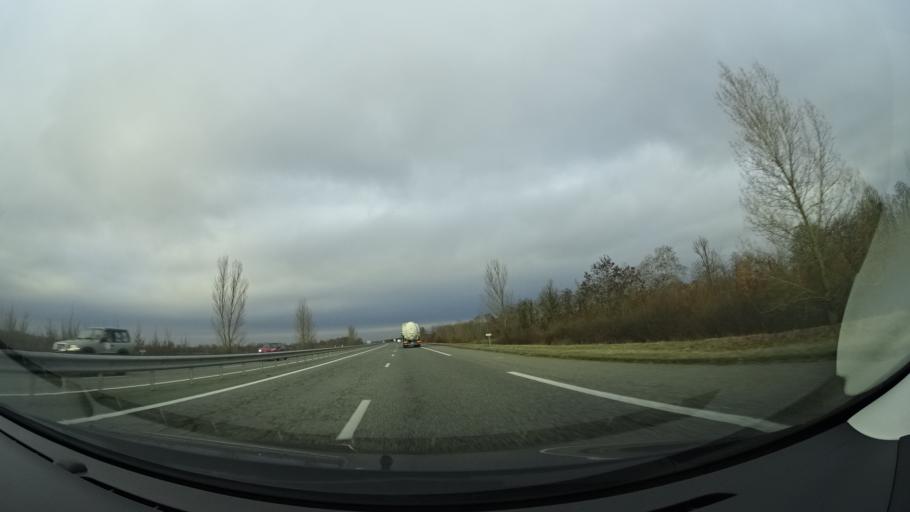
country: FR
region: Midi-Pyrenees
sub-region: Departement de l'Ariege
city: Pamiers
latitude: 43.1732
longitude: 1.6219
